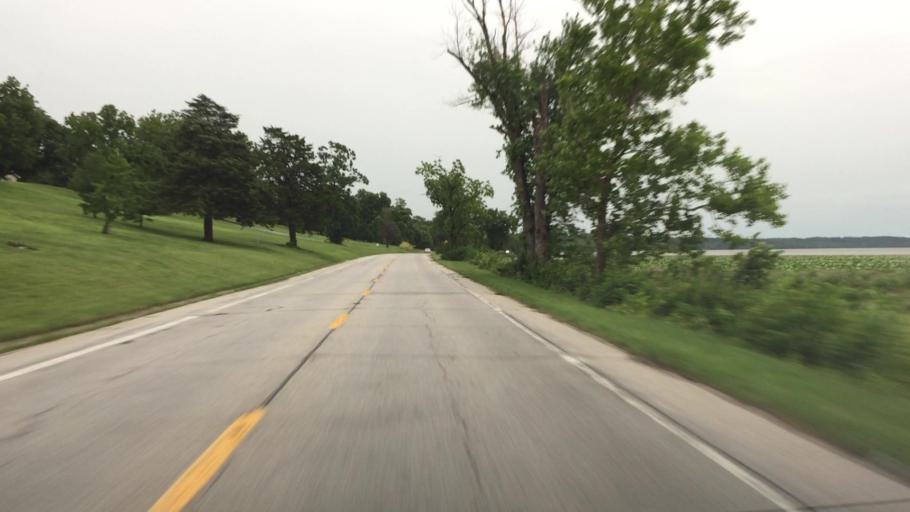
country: US
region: Illinois
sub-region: Hancock County
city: Nauvoo
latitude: 40.5289
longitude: -91.3714
